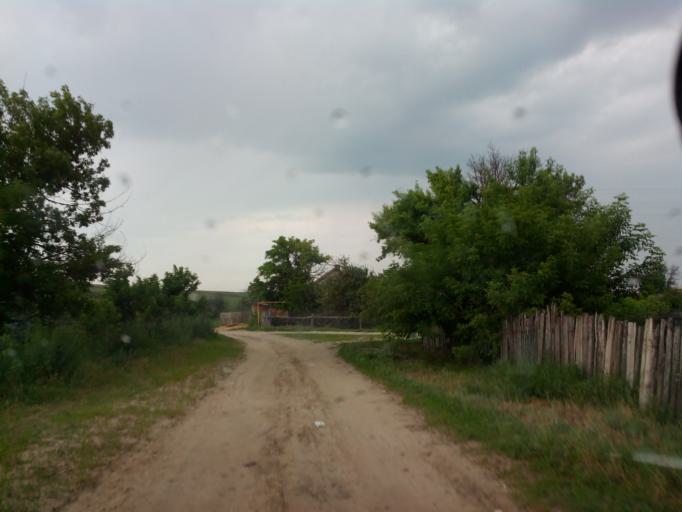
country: RU
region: Volgograd
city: Slashchevskaya
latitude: 49.7781
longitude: 42.4582
